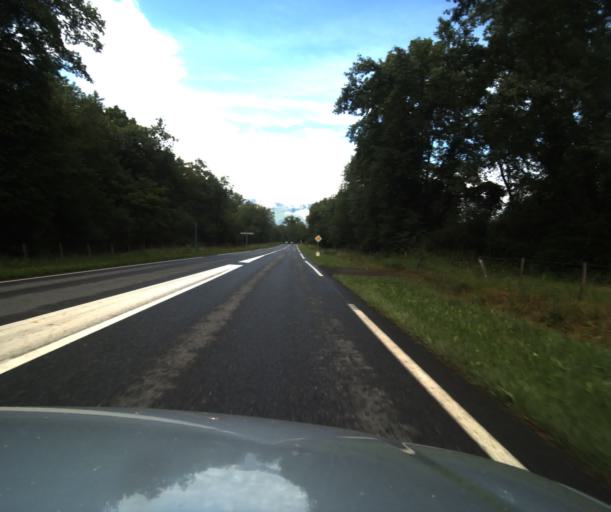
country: FR
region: Midi-Pyrenees
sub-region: Departement des Hautes-Pyrenees
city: Pierrefitte-Nestalas
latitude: 42.9714
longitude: -0.0635
